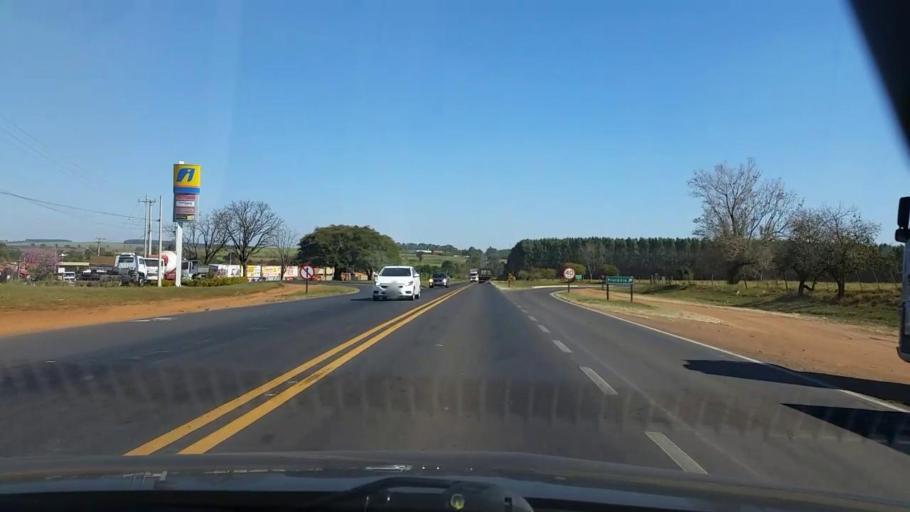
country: BR
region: Sao Paulo
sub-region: Sao Manuel
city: Sao Manuel
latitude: -22.8037
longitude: -48.6685
